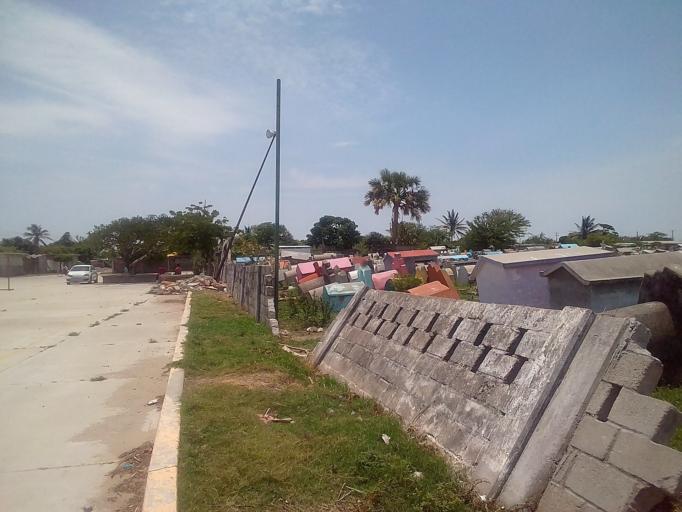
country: MX
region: Oaxaca
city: San Mateo del Mar
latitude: 16.2100
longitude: -94.9772
